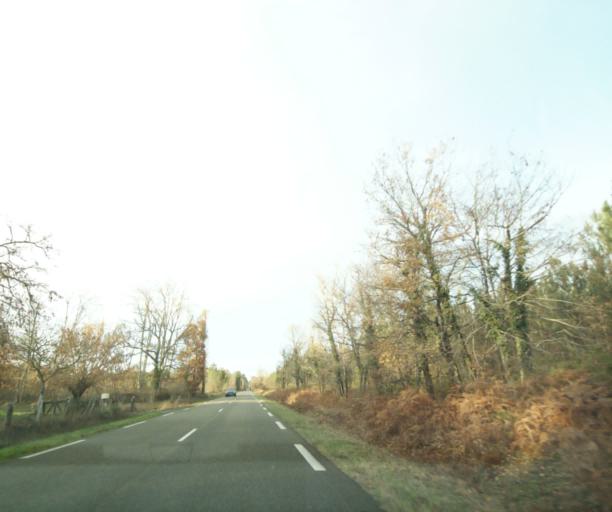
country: FR
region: Aquitaine
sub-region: Departement des Landes
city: Gabarret
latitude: 44.0508
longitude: -0.0425
